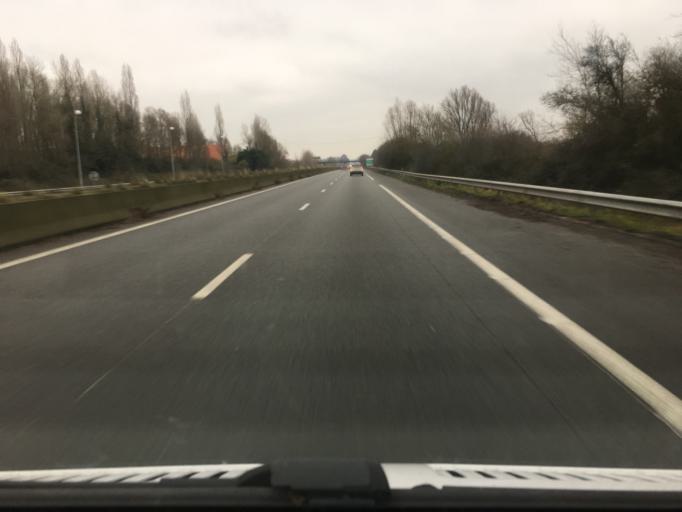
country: FR
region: Nord-Pas-de-Calais
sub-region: Departement du Nord
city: Steenvoorde
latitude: 50.8247
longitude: 2.5859
